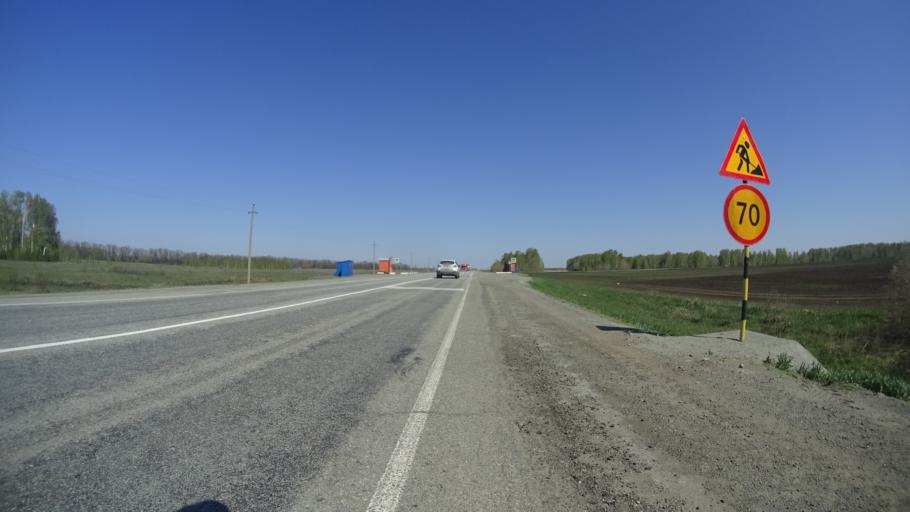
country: RU
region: Chelyabinsk
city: Troitsk
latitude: 54.1873
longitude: 61.4340
